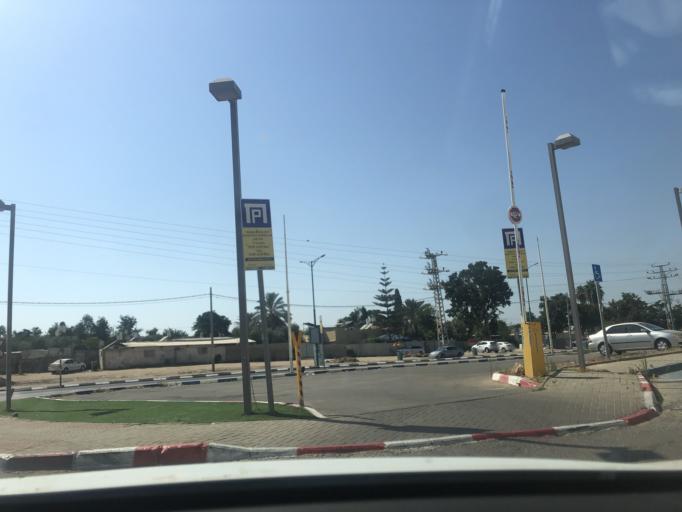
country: IL
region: Central District
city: Lod
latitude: 31.9602
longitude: 34.8993
